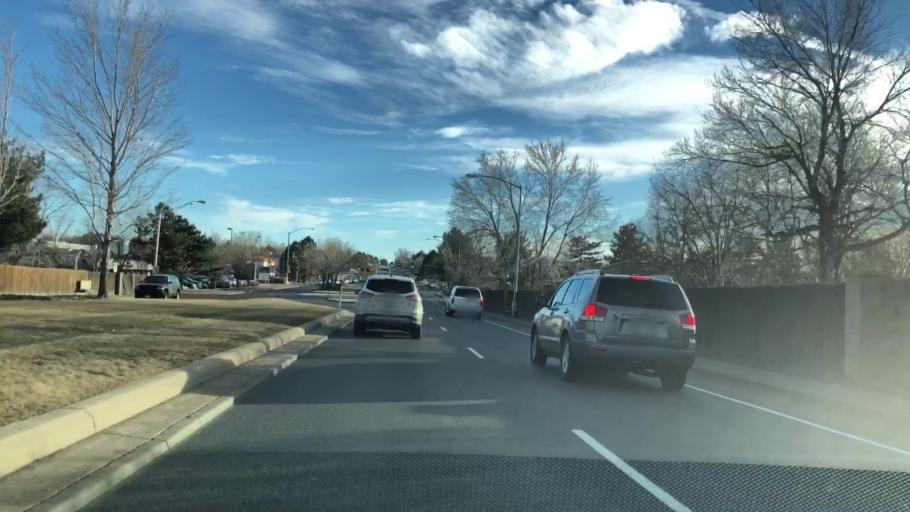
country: US
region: Colorado
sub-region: Arapahoe County
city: Dove Valley
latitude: 39.6416
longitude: -104.7917
